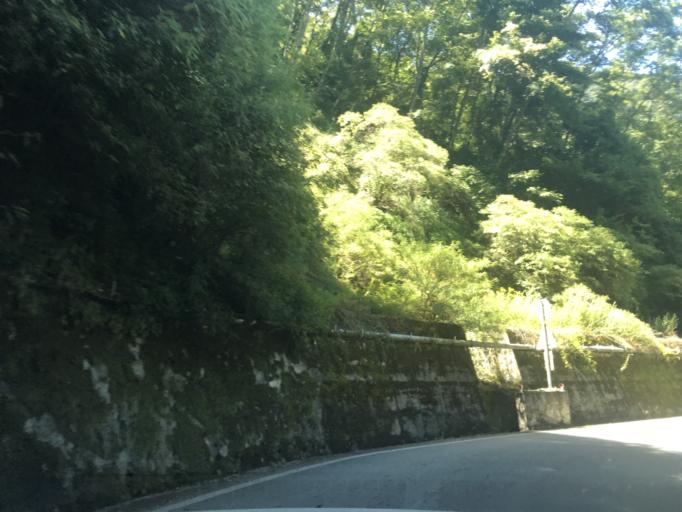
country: TW
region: Taiwan
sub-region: Nantou
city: Puli
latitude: 24.2139
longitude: 121.2677
